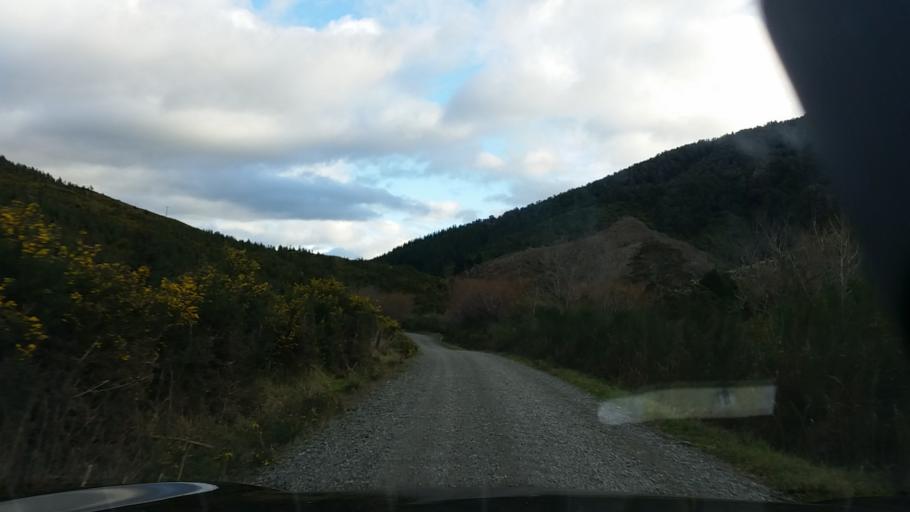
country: NZ
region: Nelson
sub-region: Nelson City
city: Nelson
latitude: -41.1831
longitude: 173.6395
